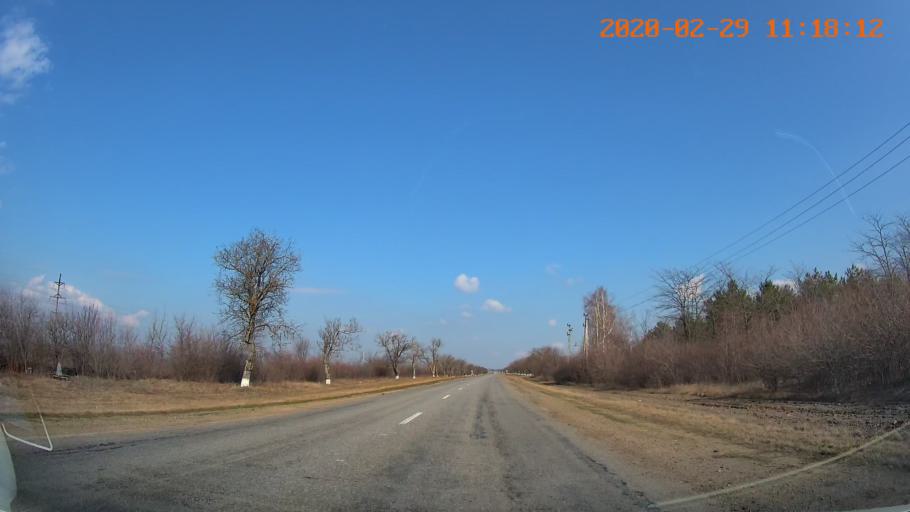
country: MD
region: Telenesti
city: Cocieri
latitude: 47.3317
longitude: 29.1722
